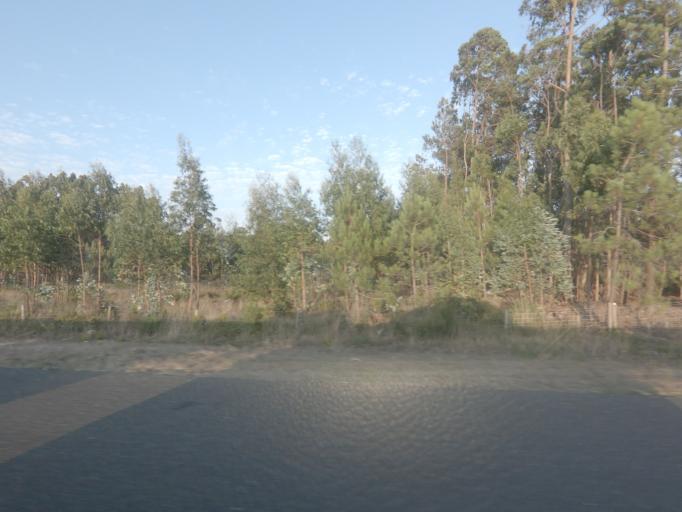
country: PT
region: Leiria
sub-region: Leiria
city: Santa Catarina da Serra
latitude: 39.6370
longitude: -8.6986
